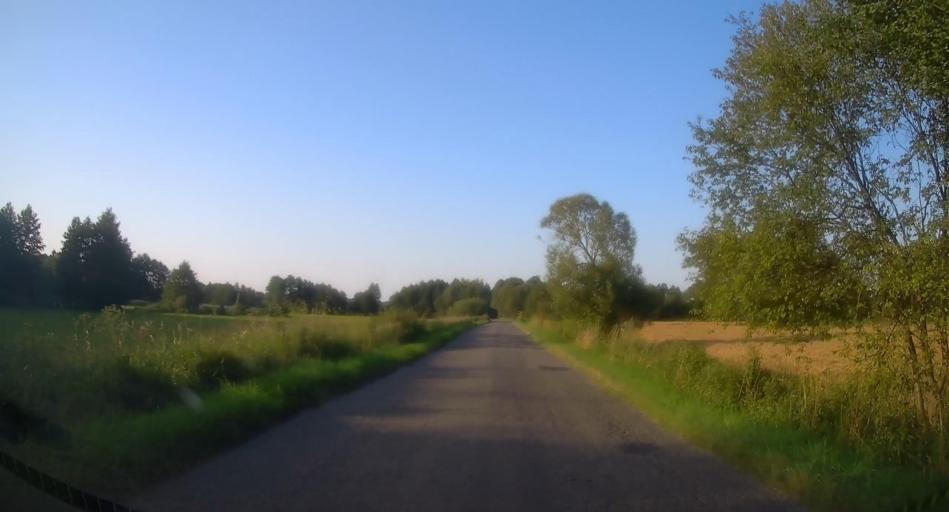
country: PL
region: Lodz Voivodeship
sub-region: Powiat skierniewicki
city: Kaweczyn Nowy
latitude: 51.8938
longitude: 20.2960
